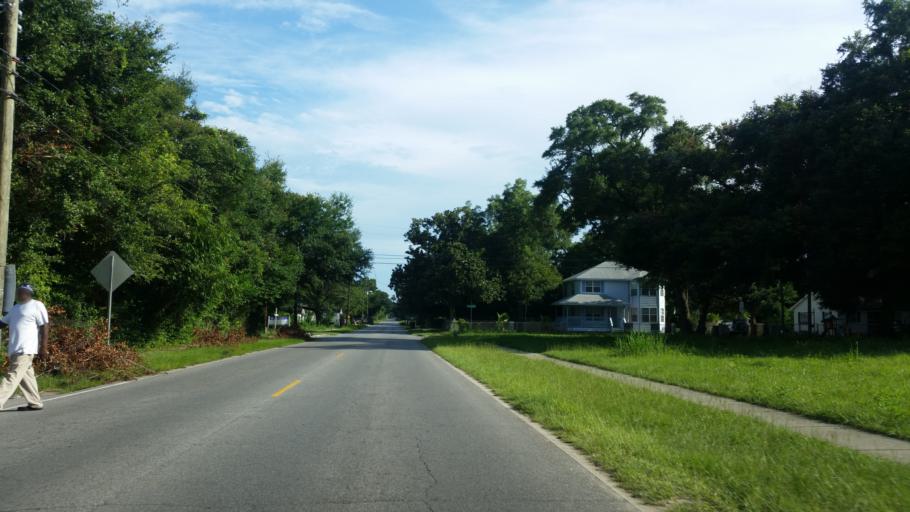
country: US
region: Florida
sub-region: Escambia County
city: Goulding
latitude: 30.4282
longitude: -87.2465
